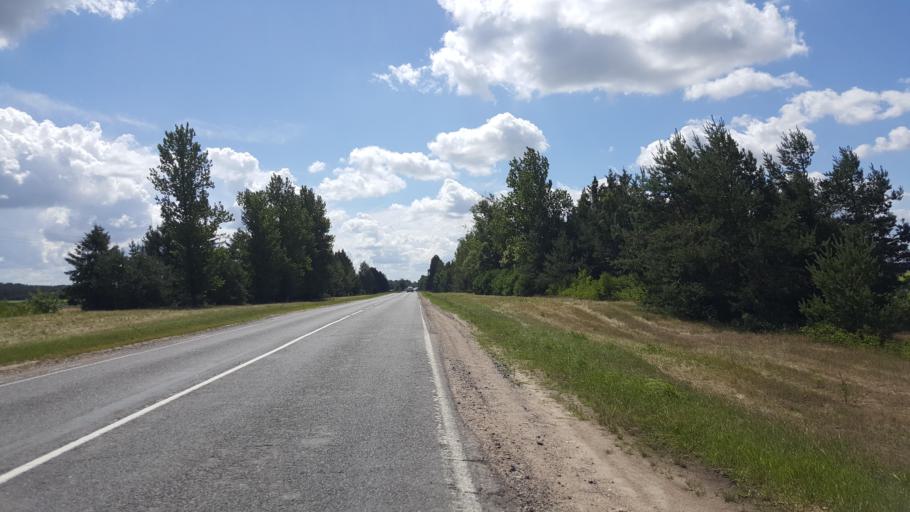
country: BY
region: Brest
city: Kamyanyets
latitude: 52.3548
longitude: 23.8964
